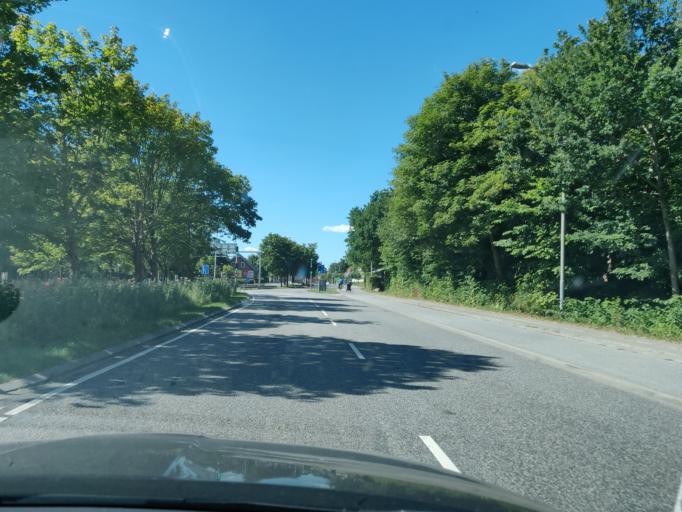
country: DK
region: North Denmark
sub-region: Alborg Kommune
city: Aalborg
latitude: 57.0643
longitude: 9.9397
